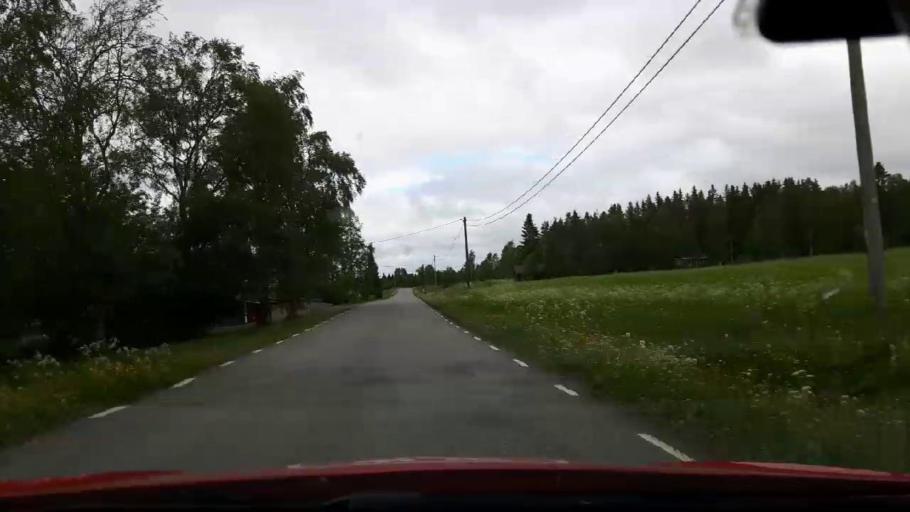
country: SE
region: Jaemtland
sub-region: Krokoms Kommun
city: Krokom
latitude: 63.2600
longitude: 14.5380
